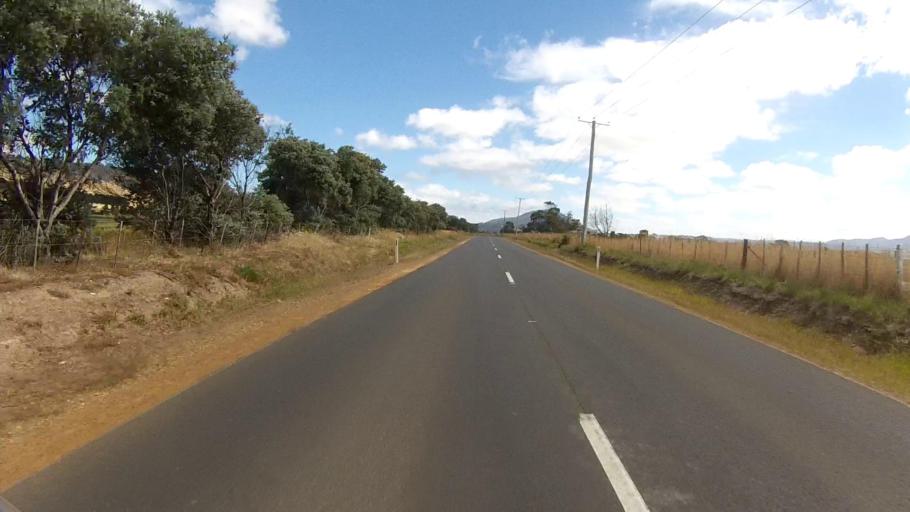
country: AU
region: Tasmania
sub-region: Clarence
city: Cambridge
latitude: -42.7154
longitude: 147.4314
